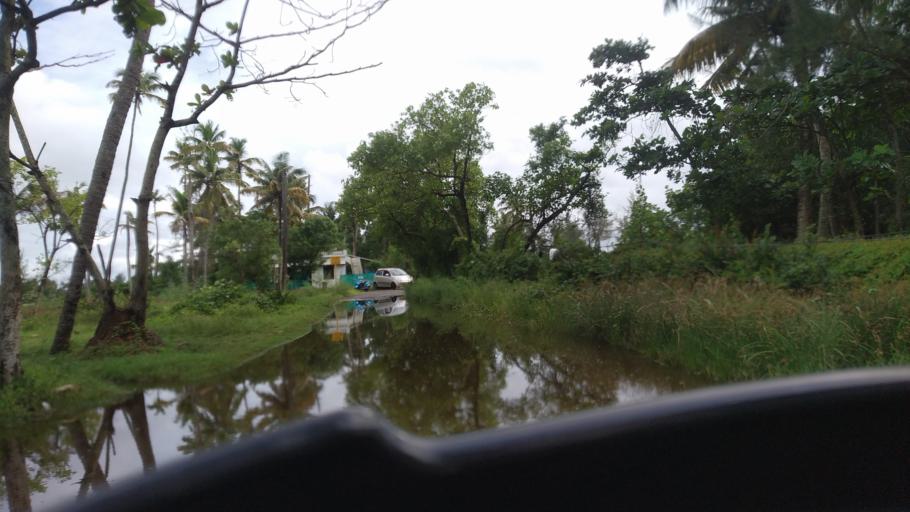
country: IN
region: Kerala
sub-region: Ernakulam
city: Elur
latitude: 10.1027
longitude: 76.1893
